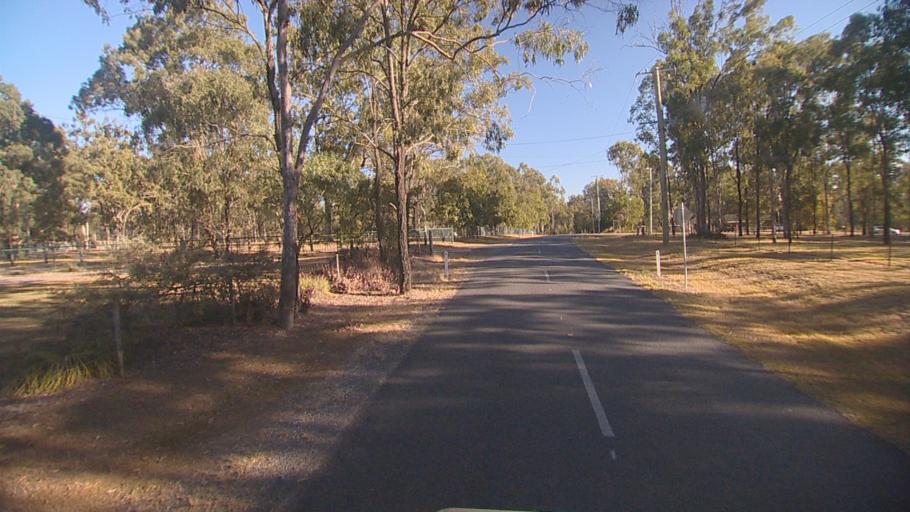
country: AU
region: Queensland
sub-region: Logan
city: North Maclean
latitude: -27.7981
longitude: 152.9935
